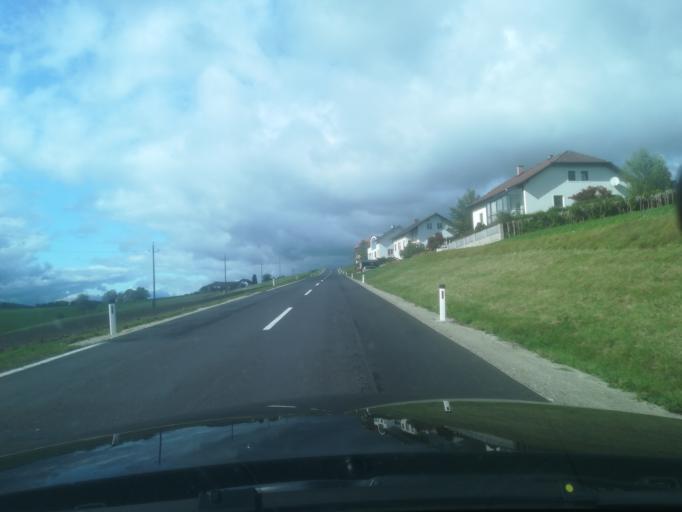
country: AT
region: Upper Austria
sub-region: Politischer Bezirk Urfahr-Umgebung
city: Gramastetten
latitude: 48.3936
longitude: 14.1840
